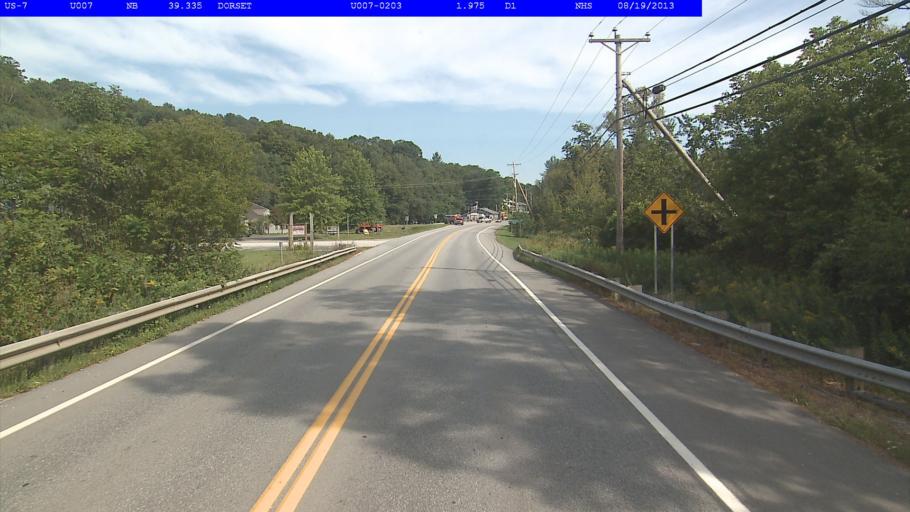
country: US
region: Vermont
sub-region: Bennington County
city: Manchester Center
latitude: 43.2376
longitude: -73.0106
